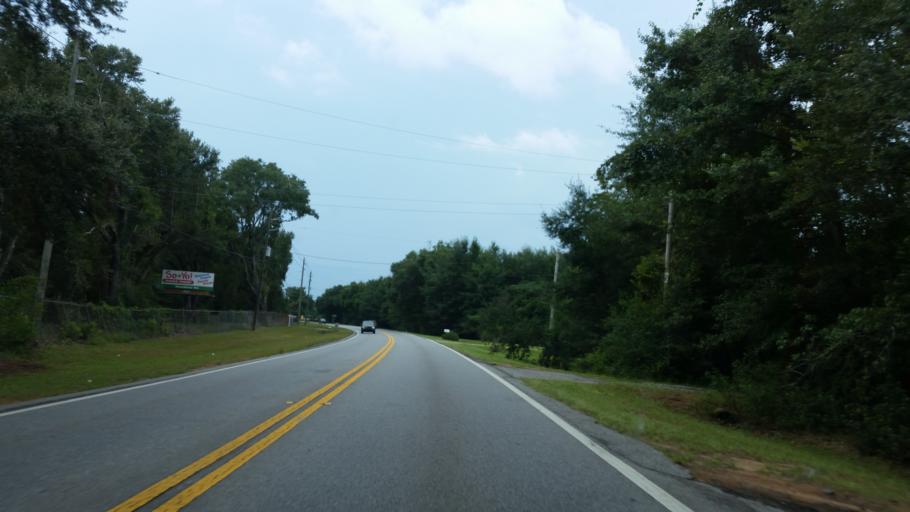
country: US
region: Florida
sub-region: Santa Rosa County
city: Pace
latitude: 30.6212
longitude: -87.1614
